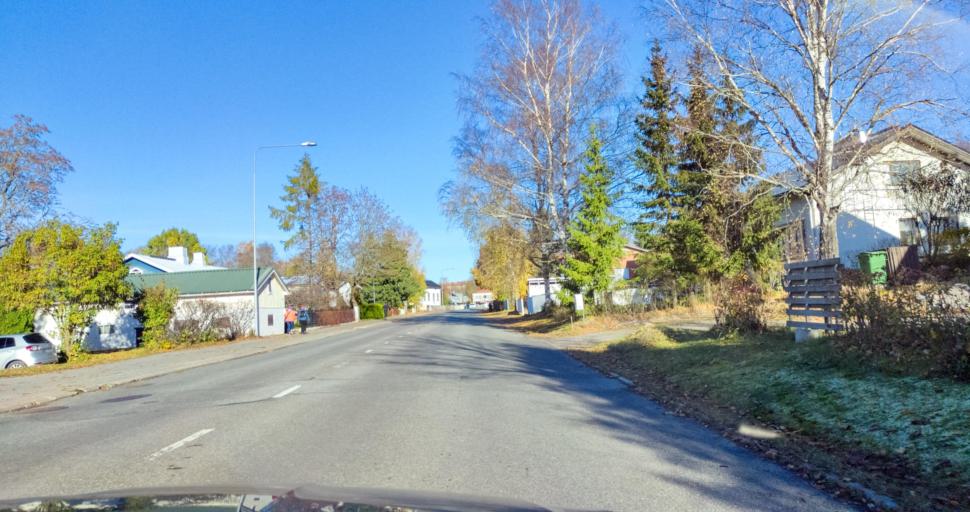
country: FI
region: Varsinais-Suomi
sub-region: Turku
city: Turku
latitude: 60.4330
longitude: 22.2581
